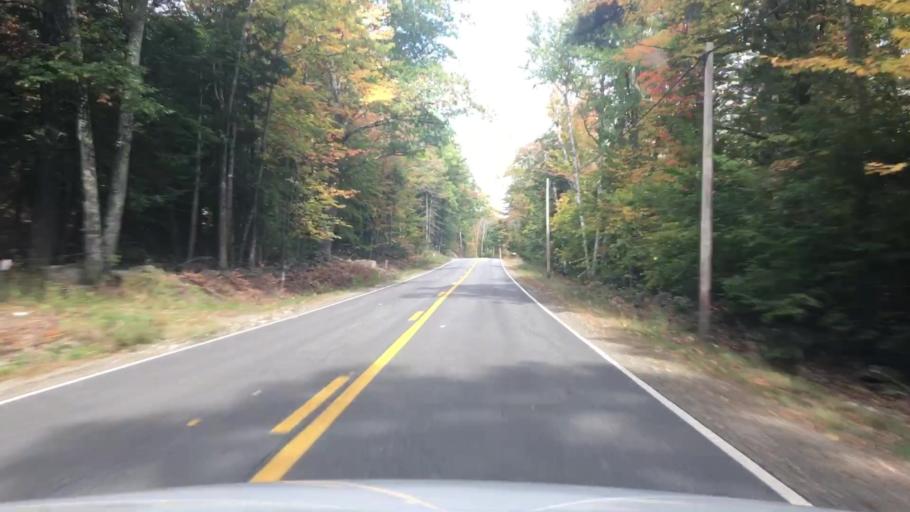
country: US
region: Maine
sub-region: Knox County
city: Hope
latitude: 44.2547
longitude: -69.1306
